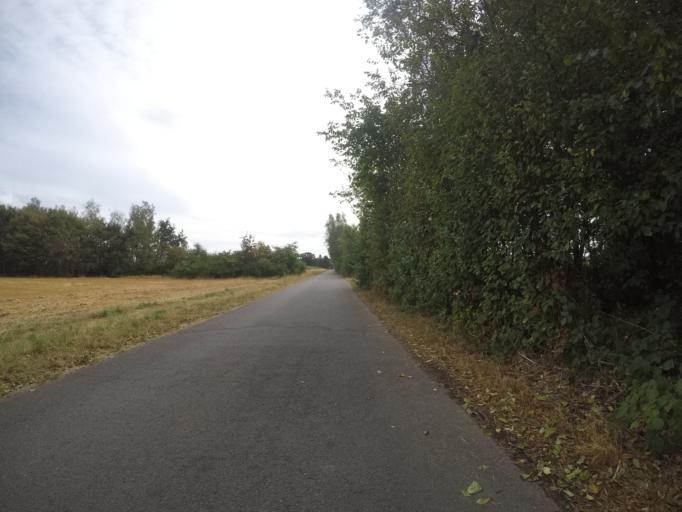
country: DE
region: North Rhine-Westphalia
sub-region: Regierungsbezirk Dusseldorf
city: Bocholt
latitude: 51.8576
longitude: 6.5720
